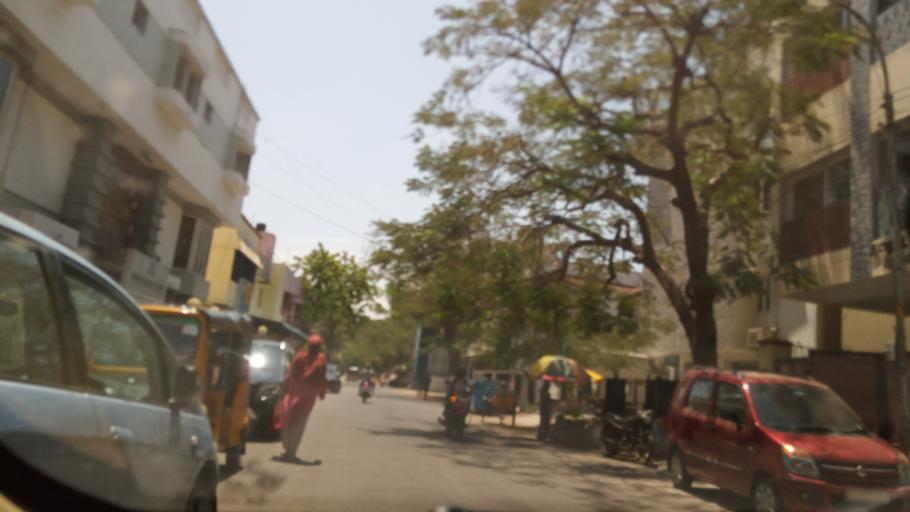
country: IN
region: Tamil Nadu
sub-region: Chennai
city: Chetput
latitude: 13.0393
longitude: 80.2236
